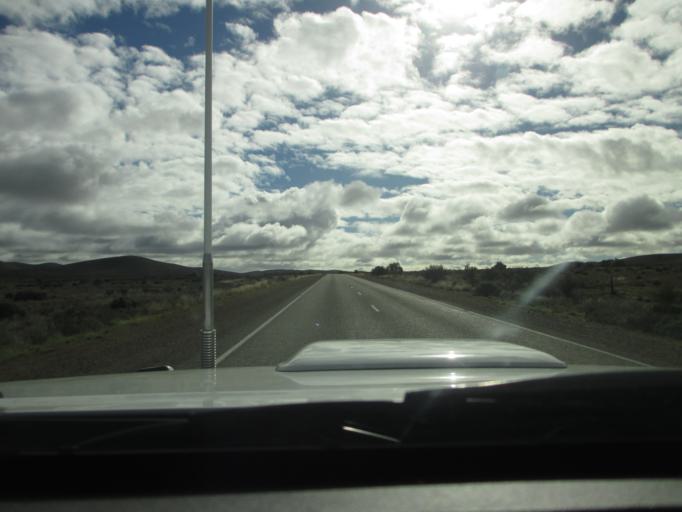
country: AU
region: South Australia
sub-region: Flinders Ranges
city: Quorn
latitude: -32.2270
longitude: 138.5161
